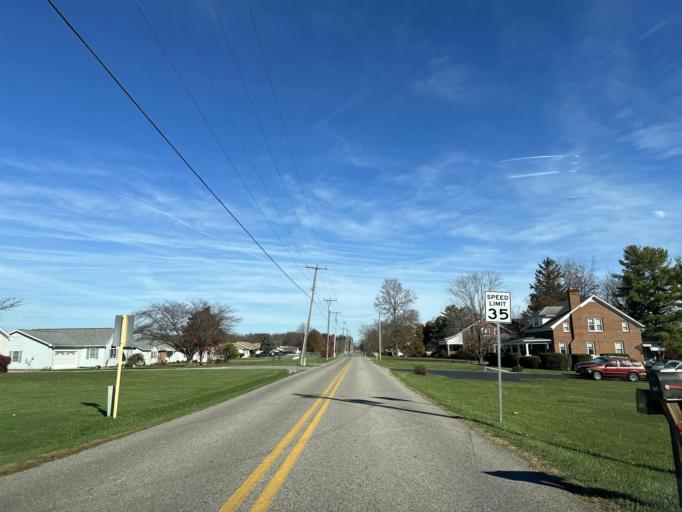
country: US
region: Virginia
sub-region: Augusta County
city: Crimora
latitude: 38.2042
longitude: -78.9040
